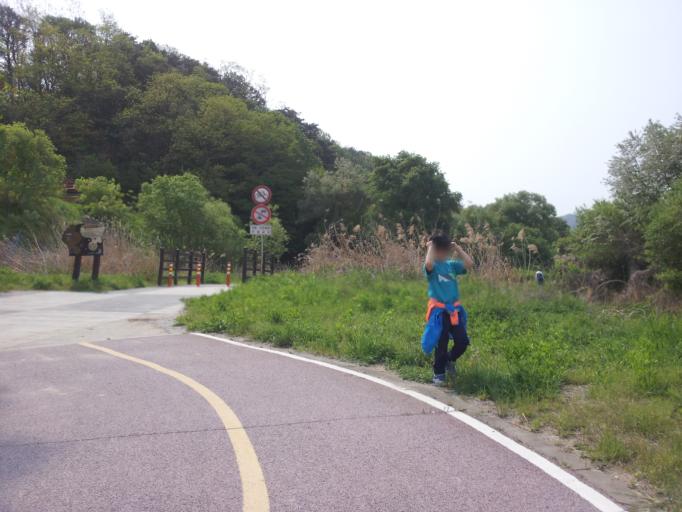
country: KR
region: Daejeon
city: Daejeon
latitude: 36.3412
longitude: 127.3531
